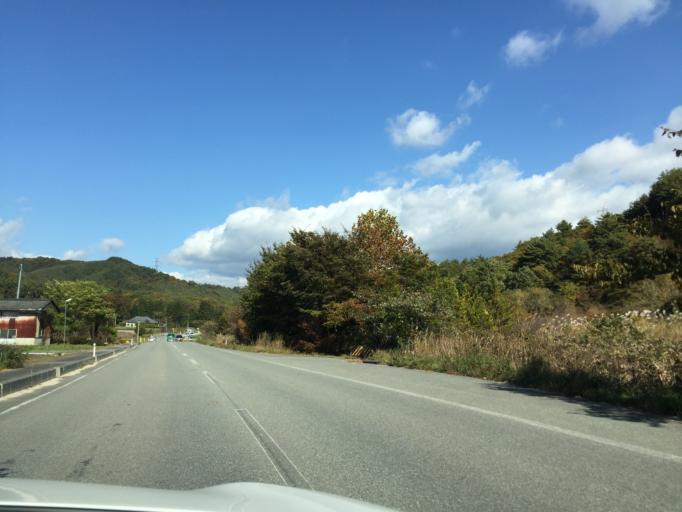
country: JP
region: Fukushima
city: Funehikimachi-funehiki
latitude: 37.3103
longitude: 140.7721
